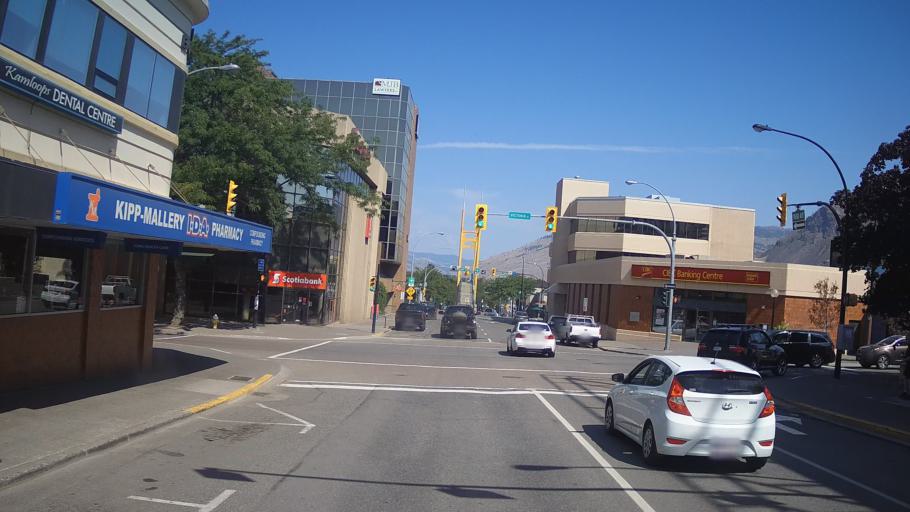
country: CA
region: British Columbia
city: Kamloops
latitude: 50.6753
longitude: -120.3347
